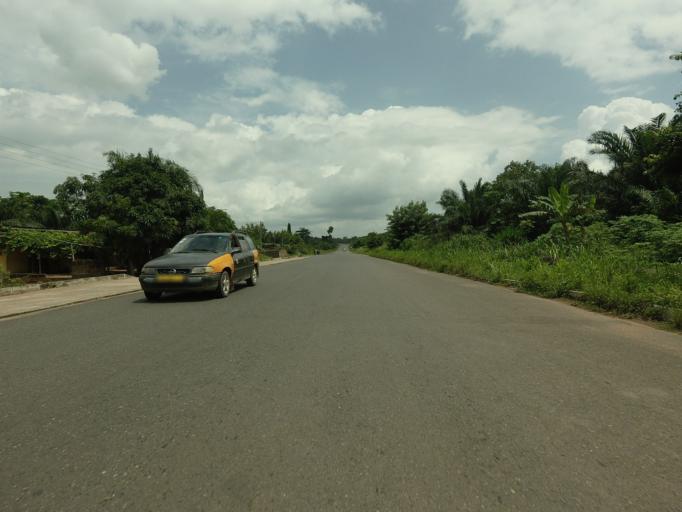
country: GH
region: Volta
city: Ho
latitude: 6.5274
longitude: 0.2248
